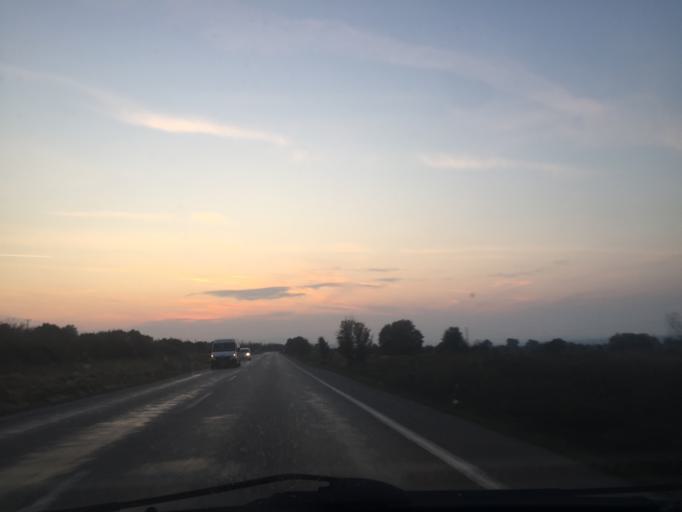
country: TR
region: Canakkale
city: Bayramic
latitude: 39.7866
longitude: 26.5228
